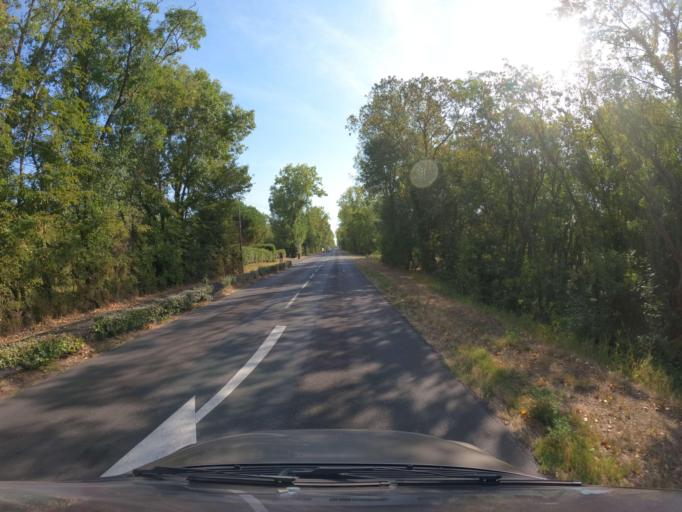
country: FR
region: Pays de la Loire
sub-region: Departement de la Vendee
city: Le Perrier
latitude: 46.8054
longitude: -2.0255
